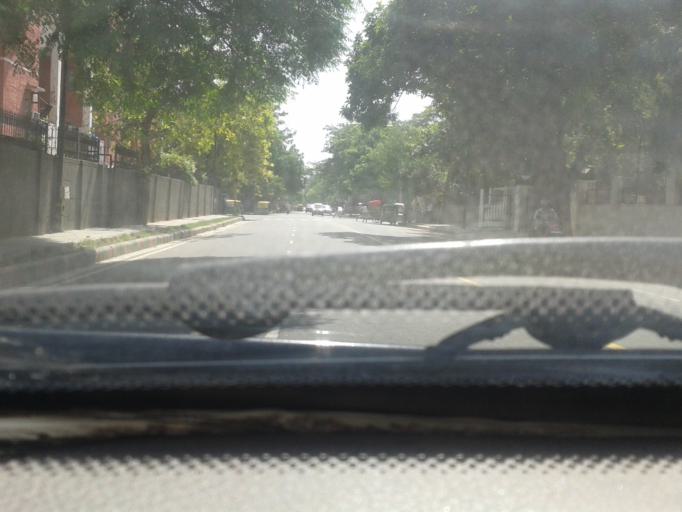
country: IN
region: NCT
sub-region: New Delhi
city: New Delhi
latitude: 28.6303
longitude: 77.2010
